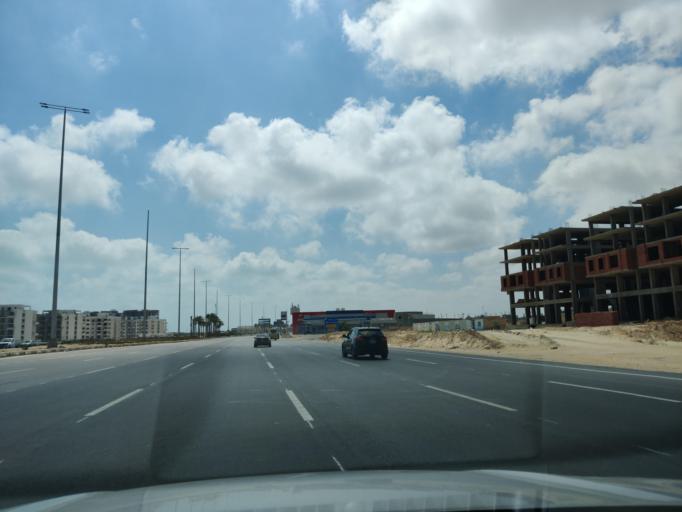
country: EG
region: Muhafazat Matruh
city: Al `Alamayn
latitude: 30.8453
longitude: 28.9383
